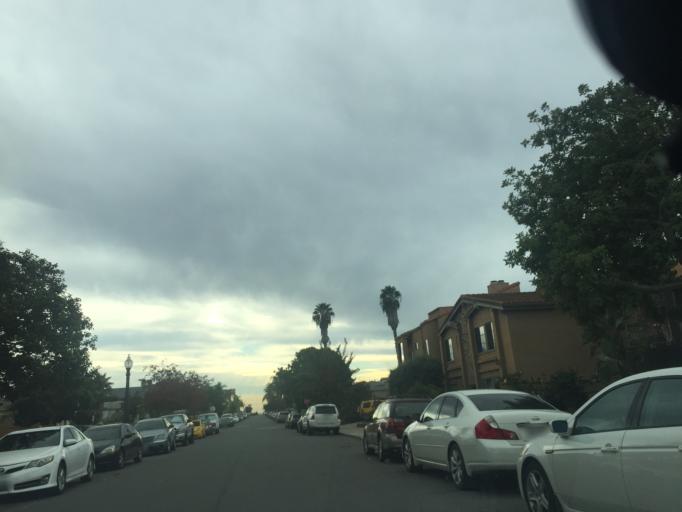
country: US
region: California
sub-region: San Diego County
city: Lemon Grove
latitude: 32.7598
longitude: -117.0846
